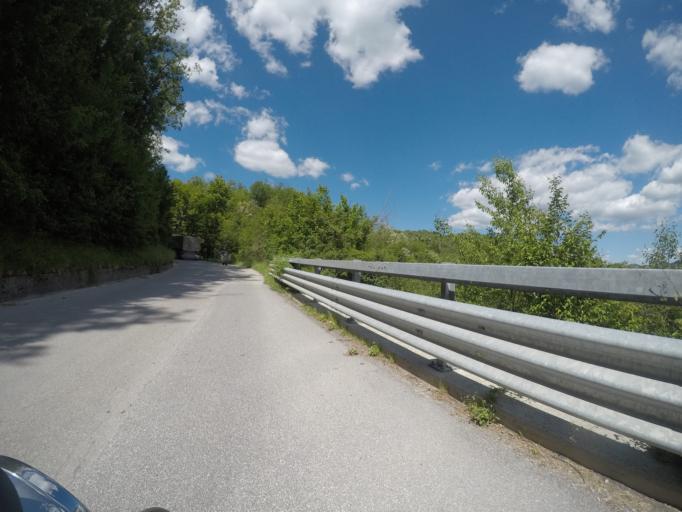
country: IT
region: Tuscany
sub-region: Provincia di Lucca
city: Minucciano
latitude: 44.1638
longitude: 10.2122
